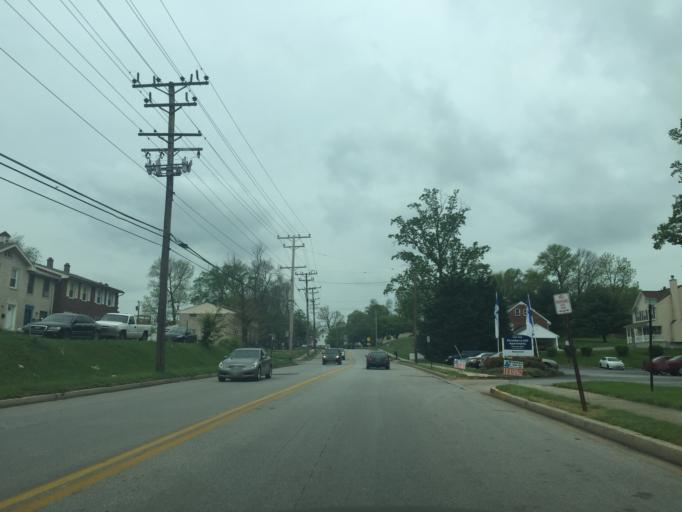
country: US
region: Maryland
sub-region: Baltimore County
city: Woodlawn
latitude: 39.3018
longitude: -76.7177
